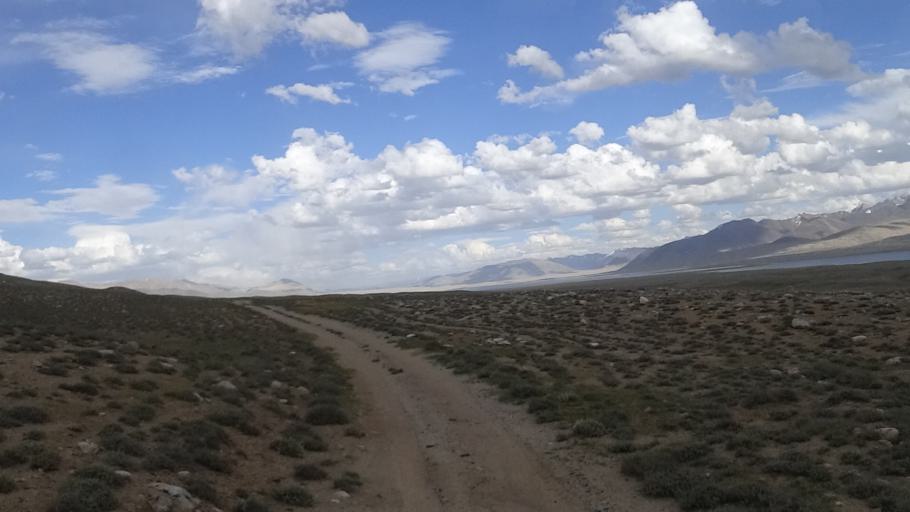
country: TJ
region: Gorno-Badakhshan
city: Murghob
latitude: 37.4680
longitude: 73.5839
